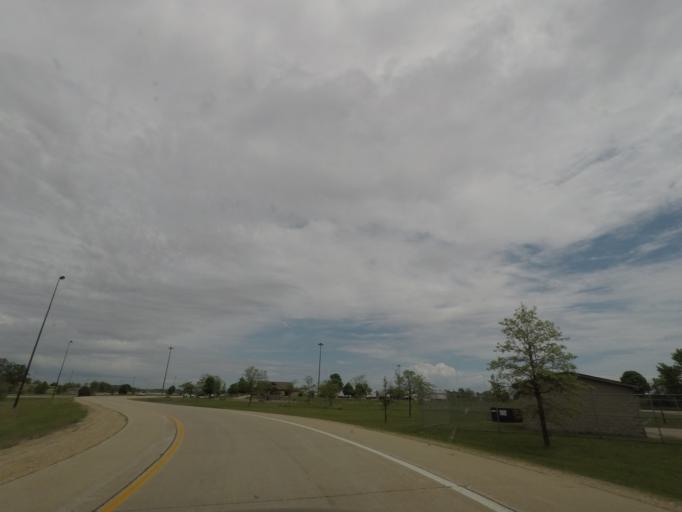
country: US
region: Illinois
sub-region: LaSalle County
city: Earlville
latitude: 41.7223
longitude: -89.0070
